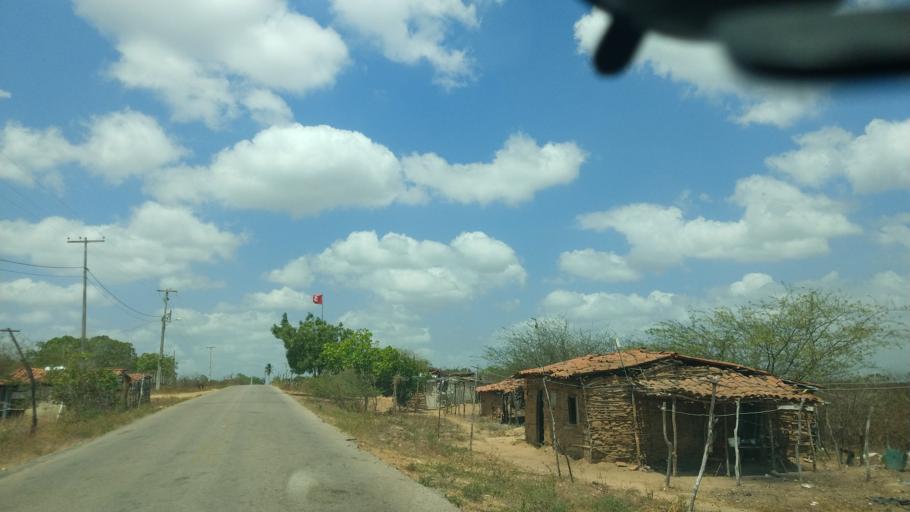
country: BR
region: Rio Grande do Norte
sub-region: Sao Paulo Do Potengi
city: Sao Paulo do Potengi
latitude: -5.9141
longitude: -35.7567
